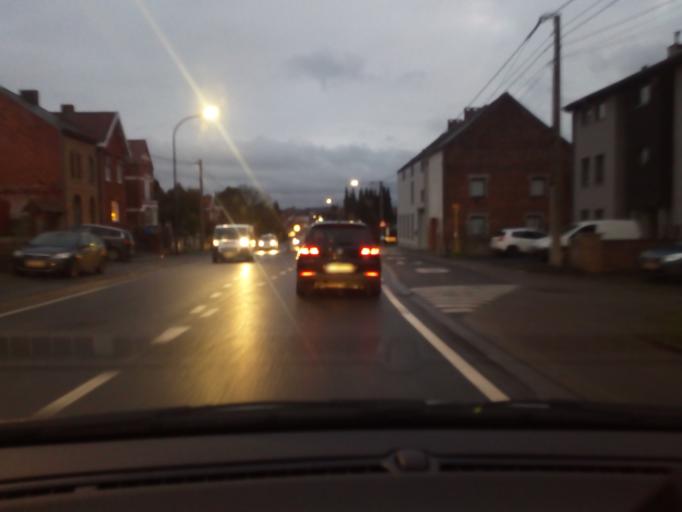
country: BE
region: Wallonia
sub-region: Province du Hainaut
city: Binche
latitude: 50.4155
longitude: 4.1492
